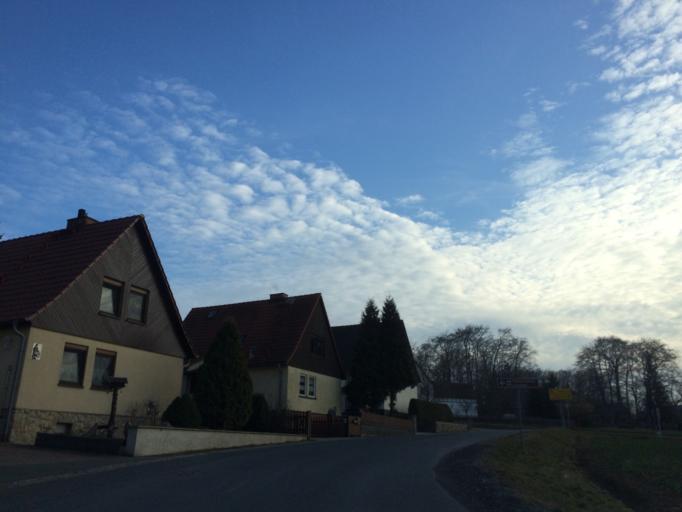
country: DE
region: Thuringia
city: Konitz
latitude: 50.6366
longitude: 11.4916
